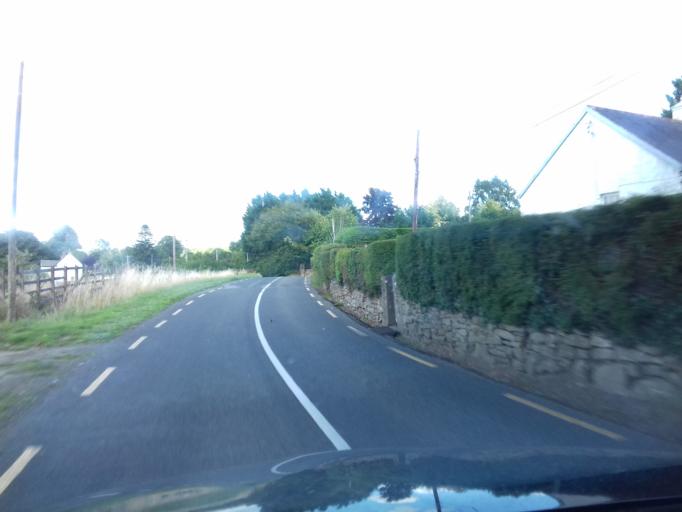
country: IE
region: Leinster
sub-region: Kilkenny
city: Thomastown
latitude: 52.5350
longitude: -7.1075
